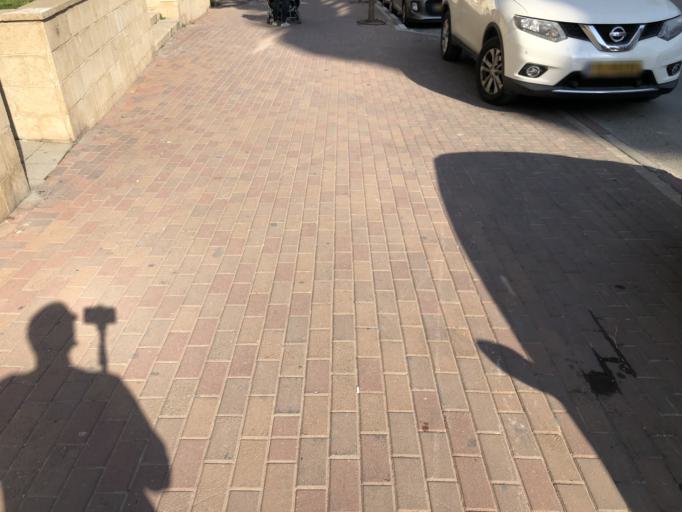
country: IL
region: Tel Aviv
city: Giv`atayim
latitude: 32.0705
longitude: 34.8125
